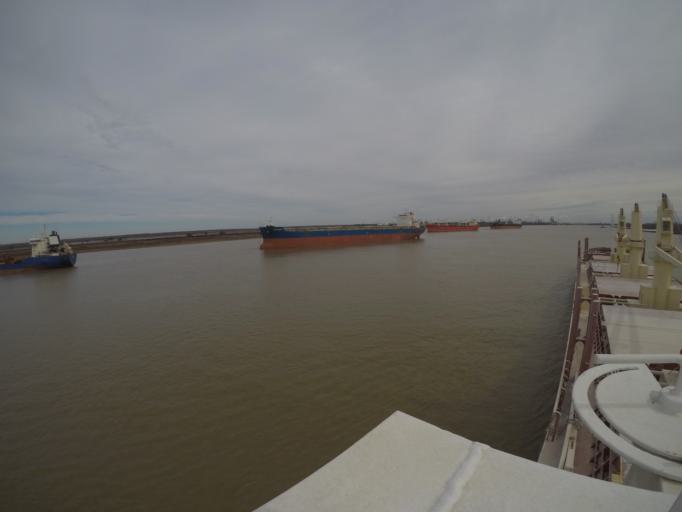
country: US
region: Louisiana
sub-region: Saint Charles Parish
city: Montz
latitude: 29.9948
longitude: -90.4444
